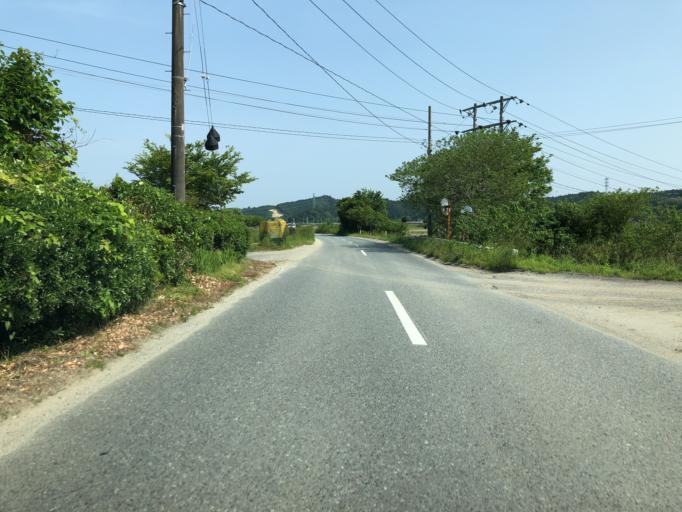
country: JP
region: Ibaraki
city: Kitaibaraki
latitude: 36.9265
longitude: 140.7425
